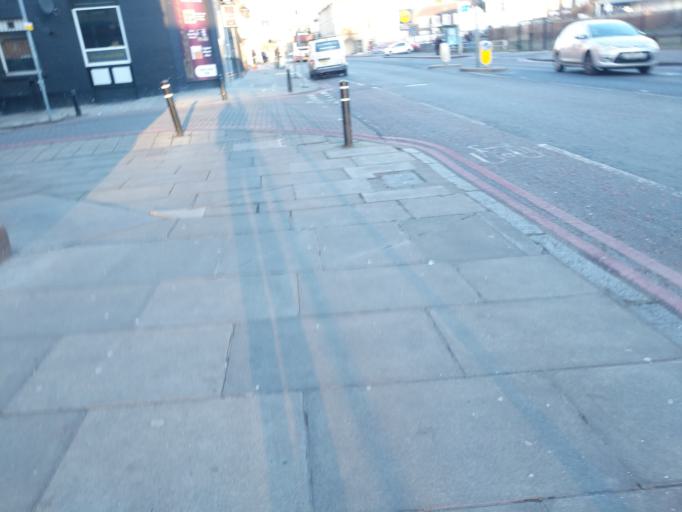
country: GB
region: Scotland
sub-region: Edinburgh
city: Edinburgh
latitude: 55.9411
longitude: -3.2238
